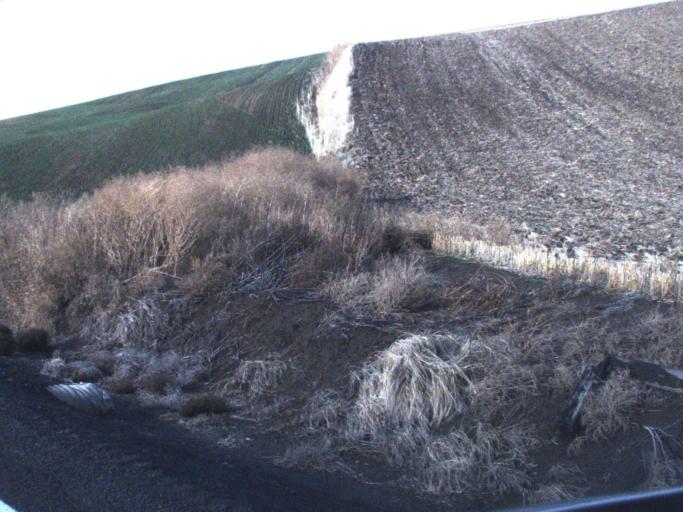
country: US
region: Washington
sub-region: Whitman County
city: Colfax
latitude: 46.7657
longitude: -117.4110
